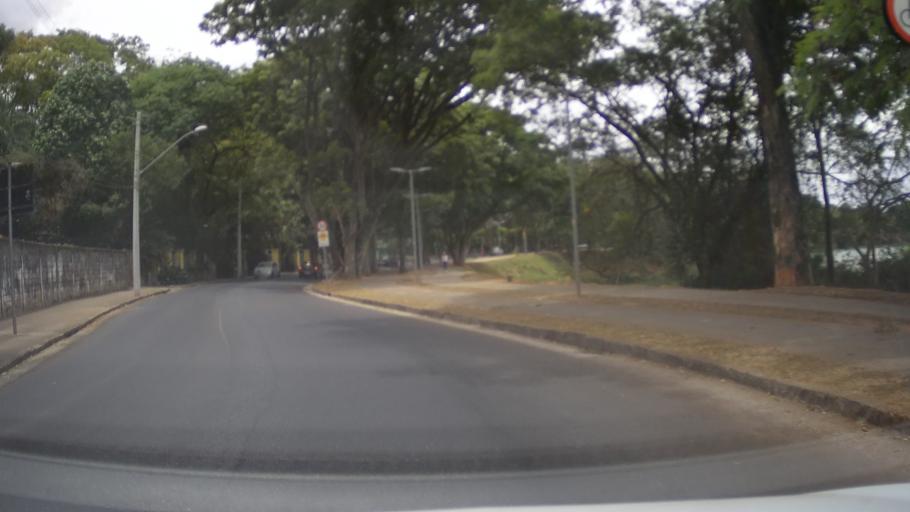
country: BR
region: Minas Gerais
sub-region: Belo Horizonte
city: Belo Horizonte
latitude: -19.8502
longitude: -43.9809
